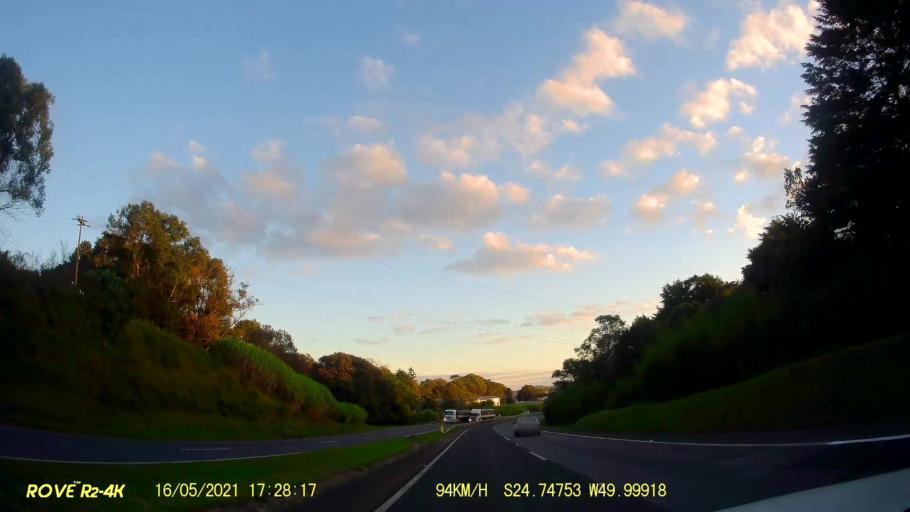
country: BR
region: Parana
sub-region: Castro
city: Castro
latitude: -24.7479
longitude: -49.9997
